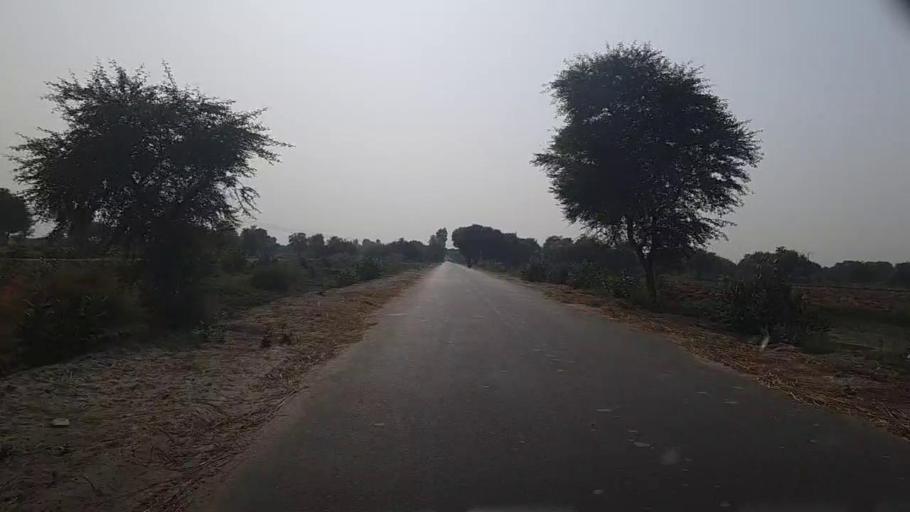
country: PK
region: Sindh
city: Kashmor
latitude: 28.3975
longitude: 69.5460
